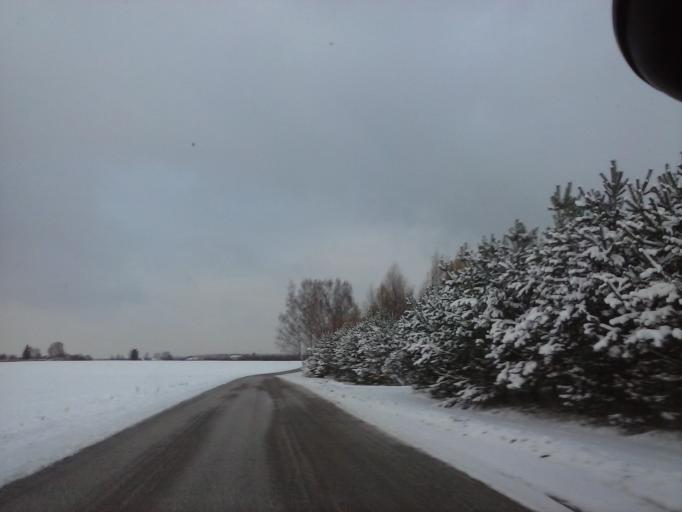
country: EE
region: Tartu
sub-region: UElenurme vald
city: Ulenurme
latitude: 58.3187
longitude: 26.8170
